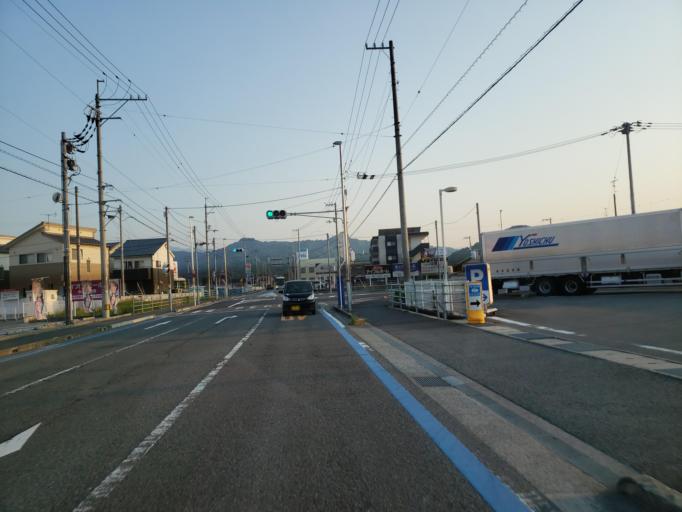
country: JP
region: Ehime
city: Hojo
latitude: 34.0386
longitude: 132.9736
